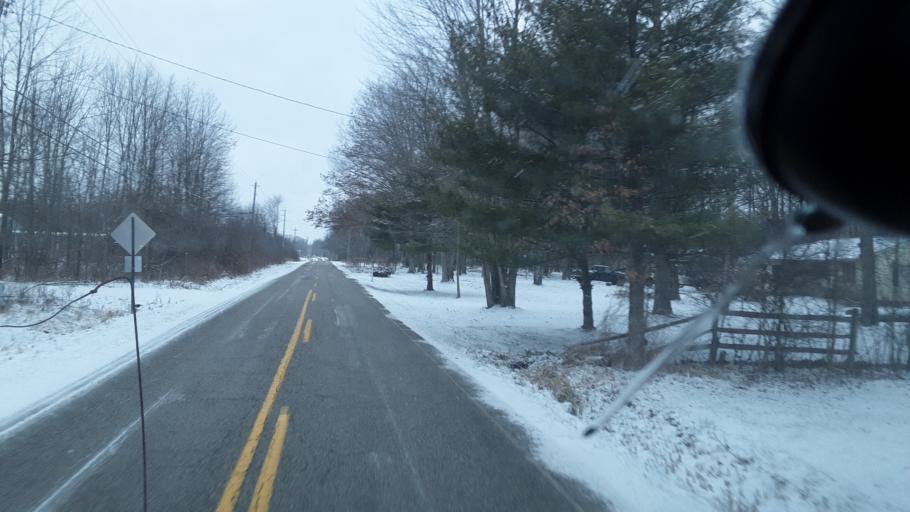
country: US
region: Ohio
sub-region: Trumbull County
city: Lordstown
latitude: 41.1290
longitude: -80.8627
